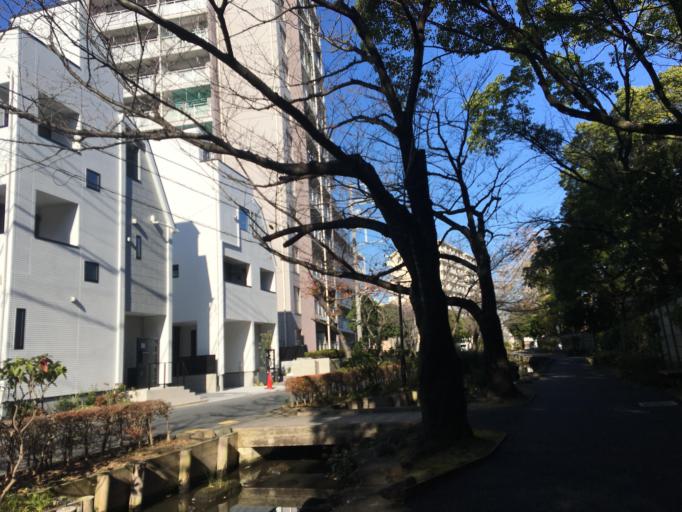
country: JP
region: Tokyo
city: Urayasu
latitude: 35.6948
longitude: 139.9110
